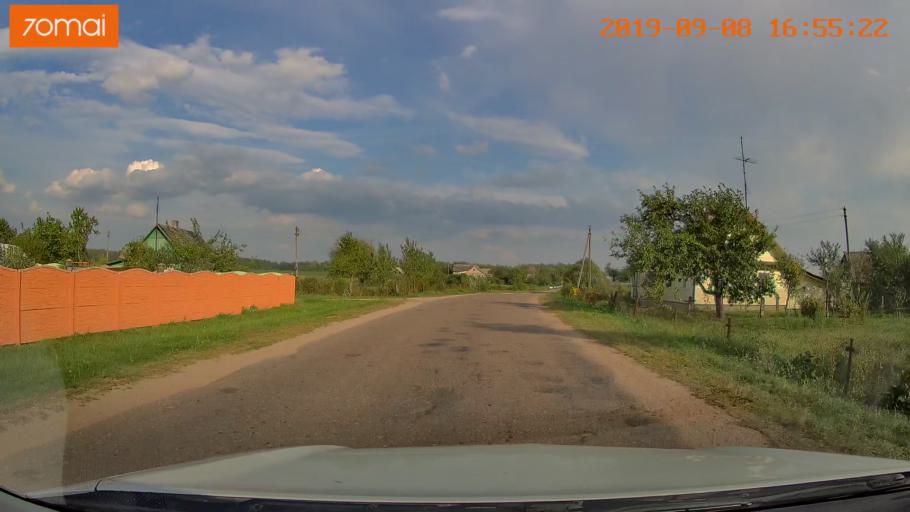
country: BY
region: Grodnenskaya
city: Hrodna
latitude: 53.7483
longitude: 23.9326
